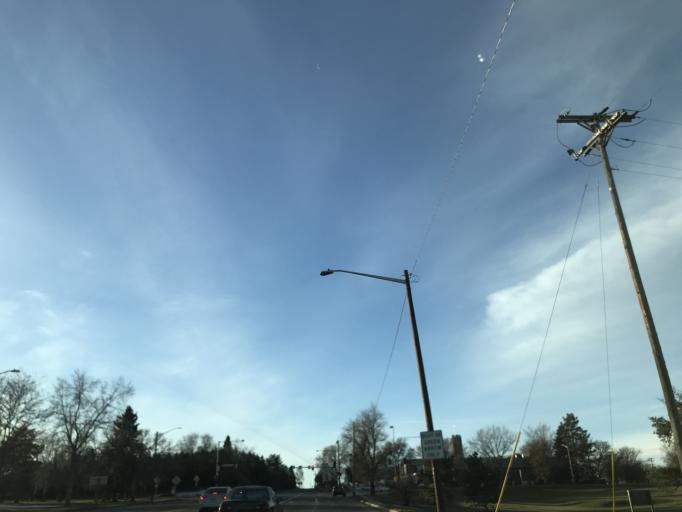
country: US
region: Colorado
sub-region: Arapahoe County
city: Cherry Hills Village
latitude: 39.6544
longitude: -104.9408
